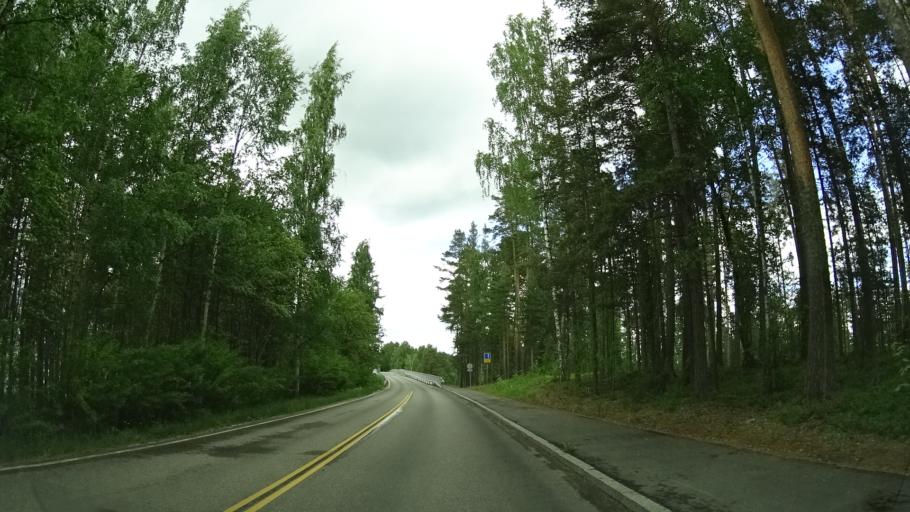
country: FI
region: Paijanne Tavastia
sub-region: Lahti
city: Asikkala
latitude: 61.3168
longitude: 25.5542
